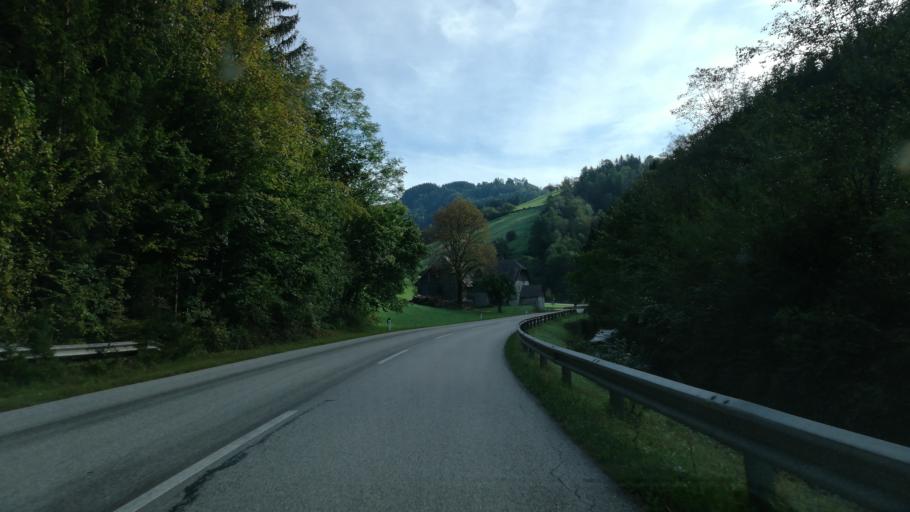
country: AT
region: Upper Austria
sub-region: Politischer Bezirk Steyr-Land
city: Maria Neustift
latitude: 47.9300
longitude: 14.6057
